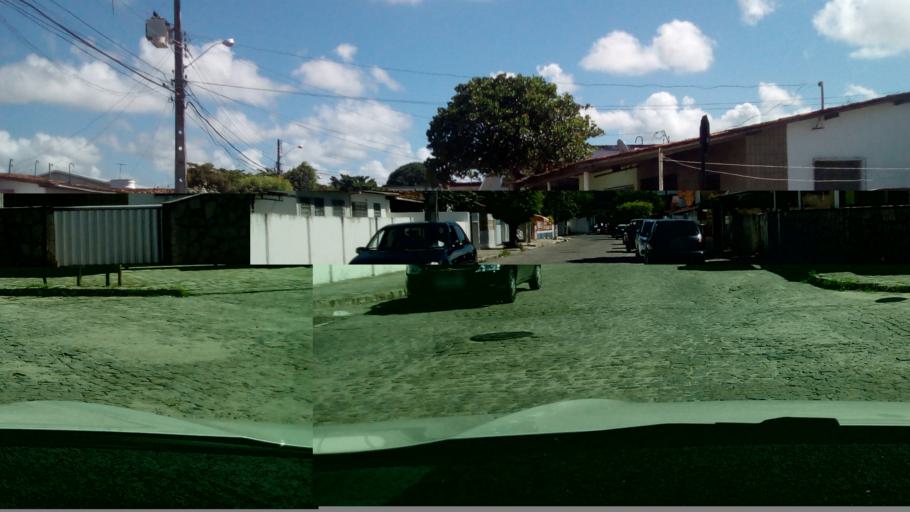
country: BR
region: Paraiba
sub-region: Joao Pessoa
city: Joao Pessoa
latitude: -7.1336
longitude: -34.8730
